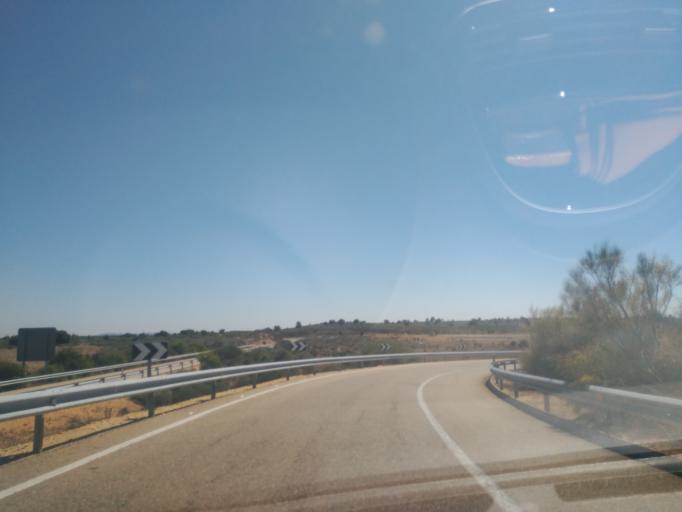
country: ES
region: Castille and Leon
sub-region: Provincia de Zamora
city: Peque
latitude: 42.0075
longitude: -6.2552
